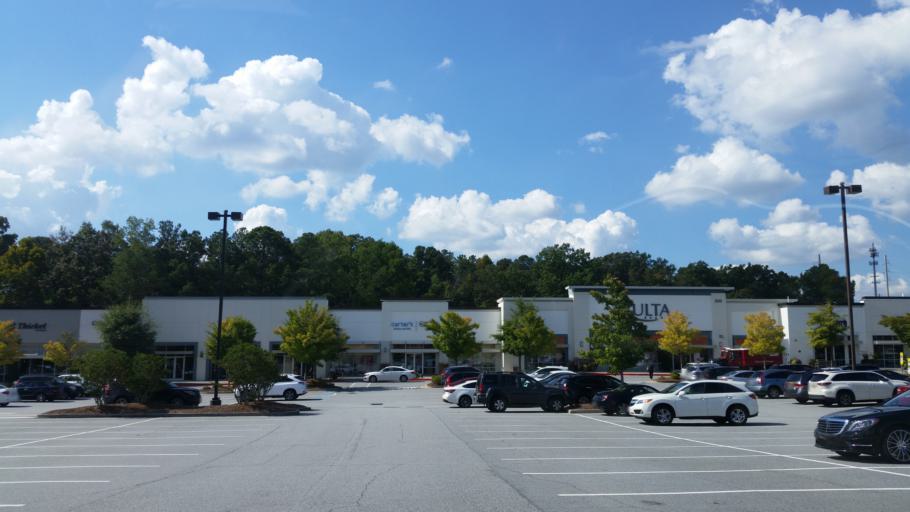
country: US
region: Georgia
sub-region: Fulton County
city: Sandy Springs
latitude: 33.9798
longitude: -84.4273
